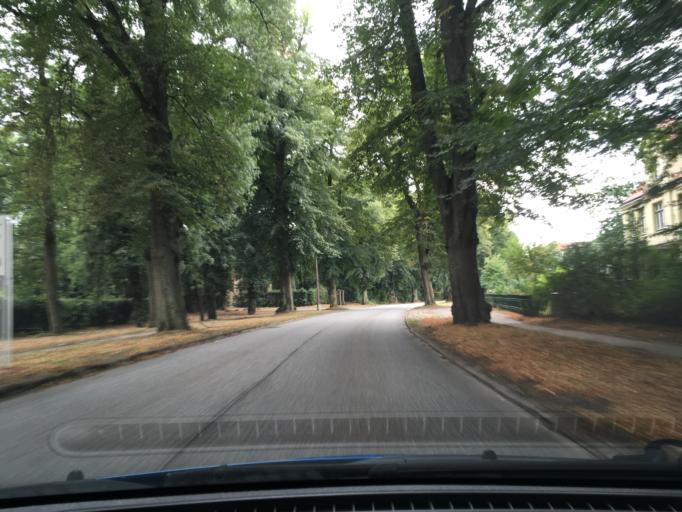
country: DE
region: Mecklenburg-Vorpommern
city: Wittenburg
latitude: 53.5050
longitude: 11.0779
